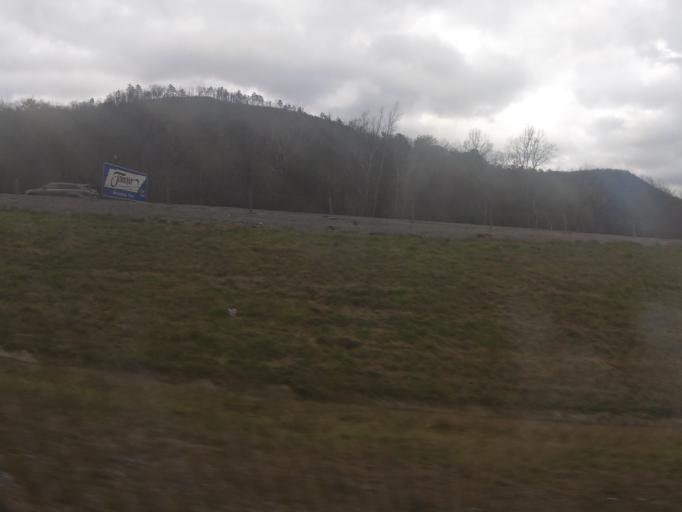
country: US
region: Georgia
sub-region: Walker County
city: Lookout Mountain
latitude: 34.9860
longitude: -85.4689
